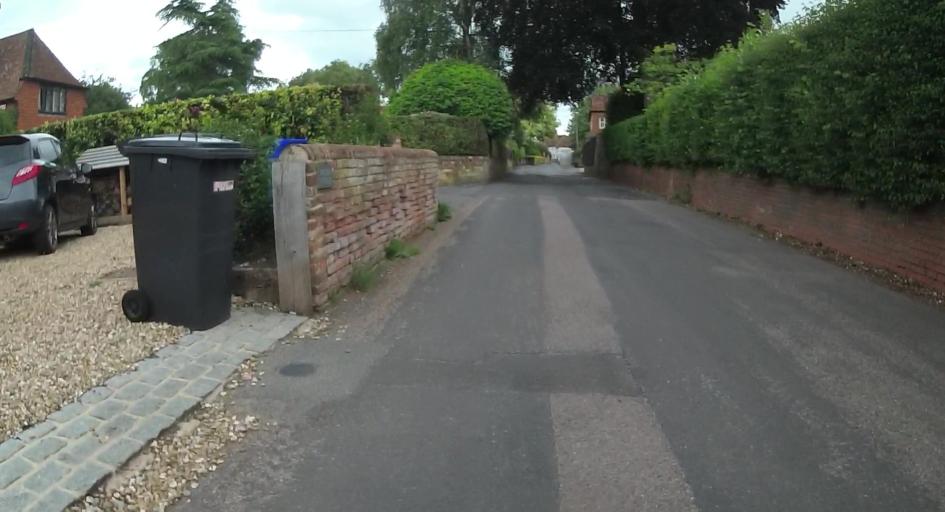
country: GB
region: England
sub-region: Hampshire
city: Fleet
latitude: 51.2326
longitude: -0.8606
